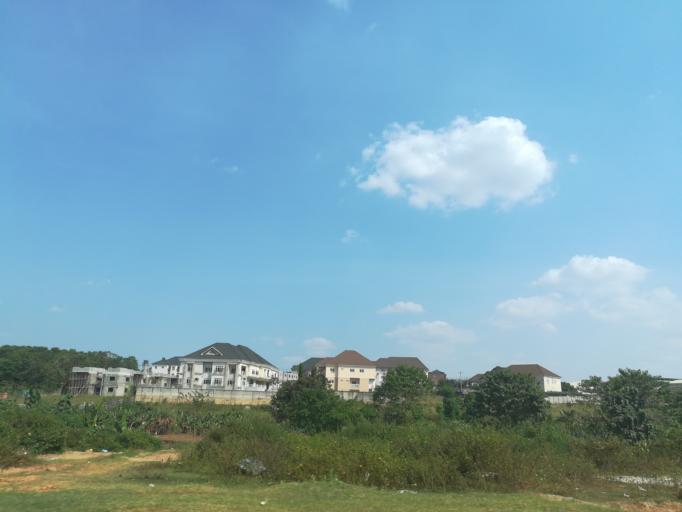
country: NG
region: Abuja Federal Capital Territory
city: Abuja
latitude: 9.0569
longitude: 7.4345
